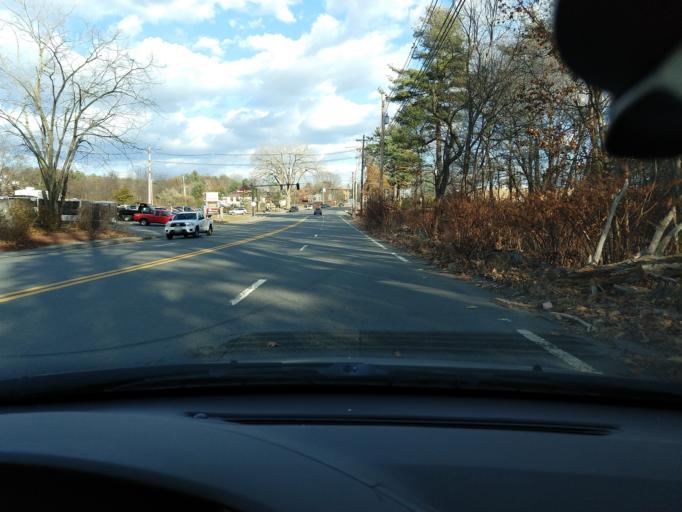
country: US
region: Massachusetts
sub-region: Middlesex County
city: Littleton Common
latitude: 42.5541
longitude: -71.4497
